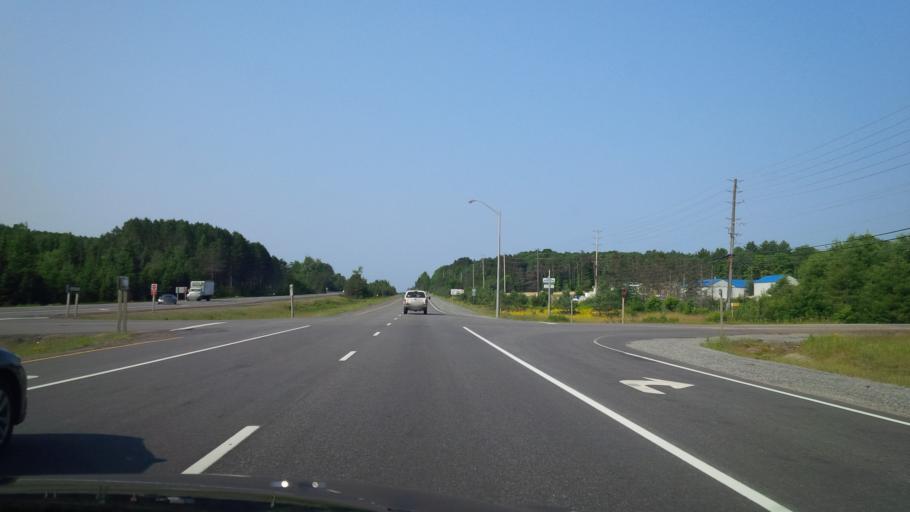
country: CA
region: Ontario
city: Huntsville
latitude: 45.2918
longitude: -79.2664
